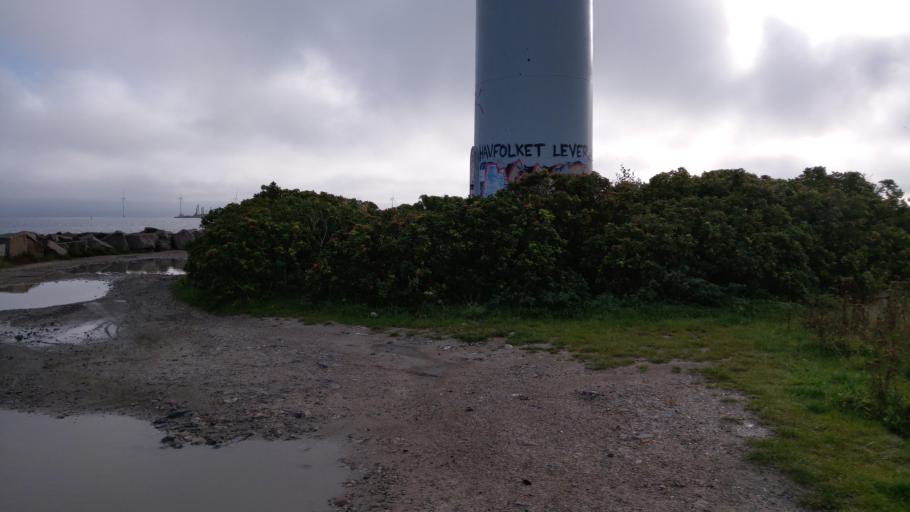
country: DK
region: Capital Region
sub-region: Kobenhavn
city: Christianshavn
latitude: 55.6973
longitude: 12.6289
